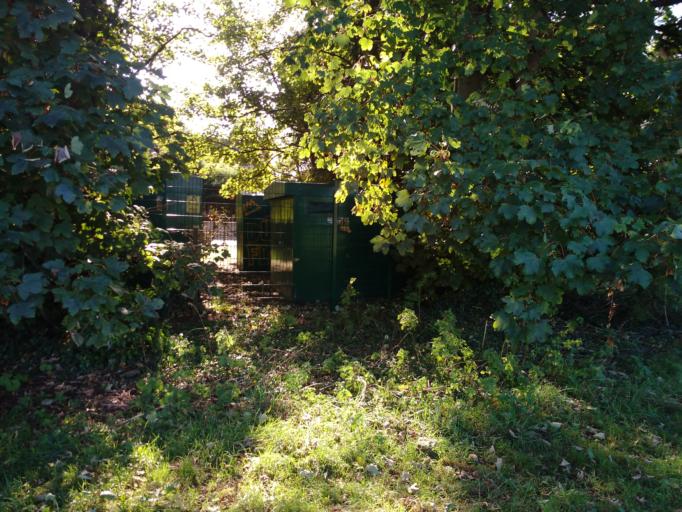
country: GB
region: England
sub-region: Bristol
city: Bristol
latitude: 51.4845
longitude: -2.6349
